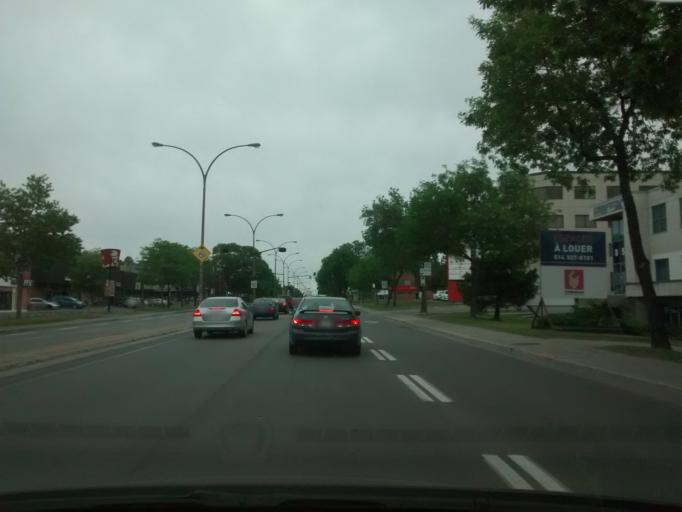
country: CA
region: Quebec
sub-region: Montreal
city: Saint-Leonard
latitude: 45.5758
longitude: -73.6124
